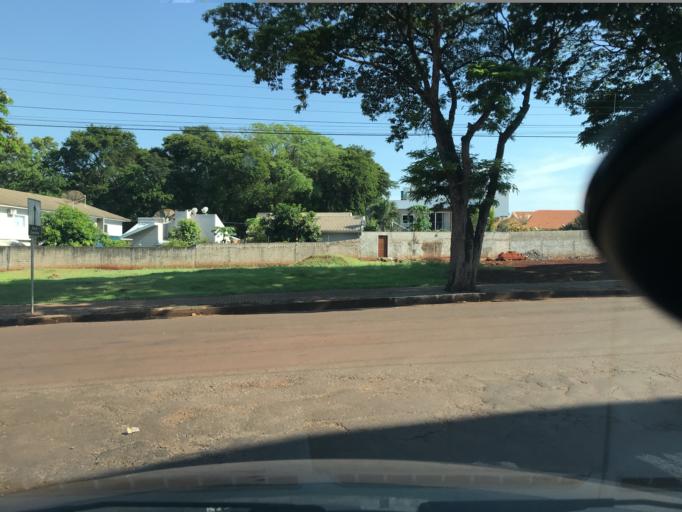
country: BR
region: Parana
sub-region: Palotina
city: Palotina
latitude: -24.2788
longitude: -53.8439
